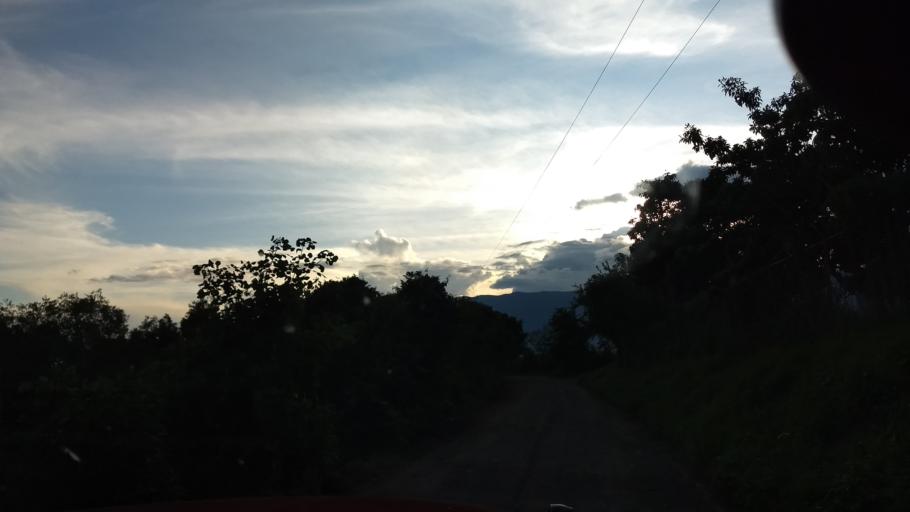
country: MX
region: Colima
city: Suchitlan
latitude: 19.4993
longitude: -103.7675
